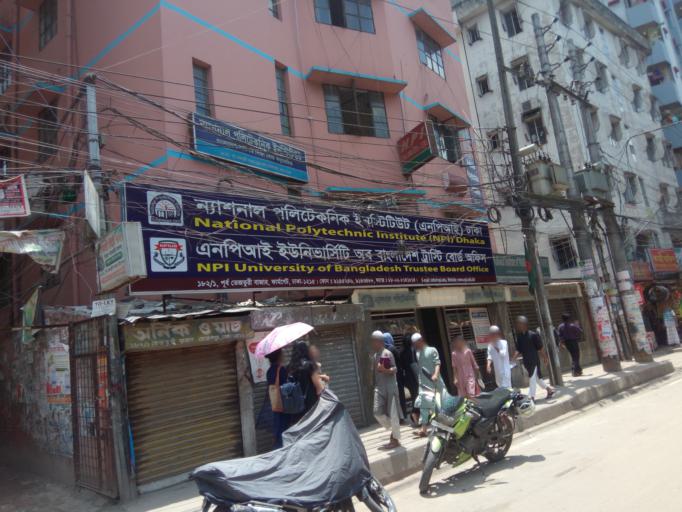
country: BD
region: Dhaka
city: Azimpur
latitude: 23.7572
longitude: 90.3930
